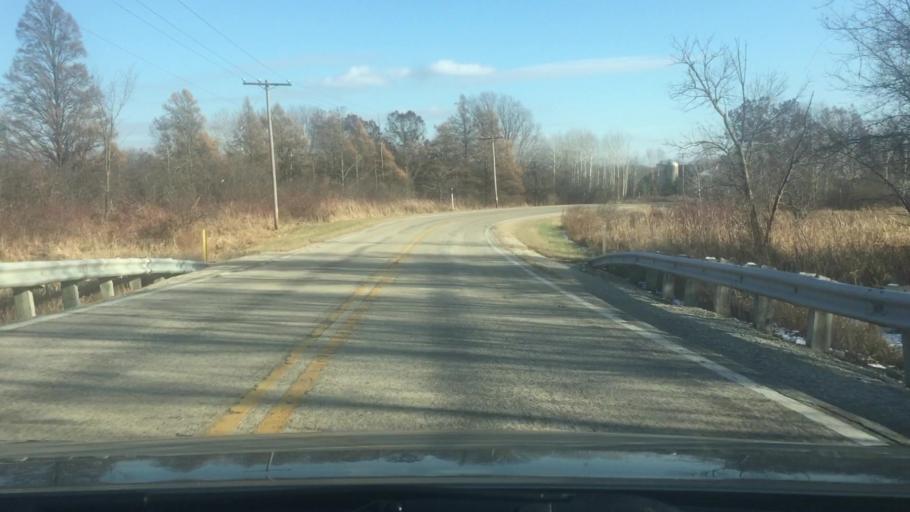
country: US
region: Wisconsin
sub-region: Jefferson County
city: Palmyra
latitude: 42.9395
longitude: -88.5920
